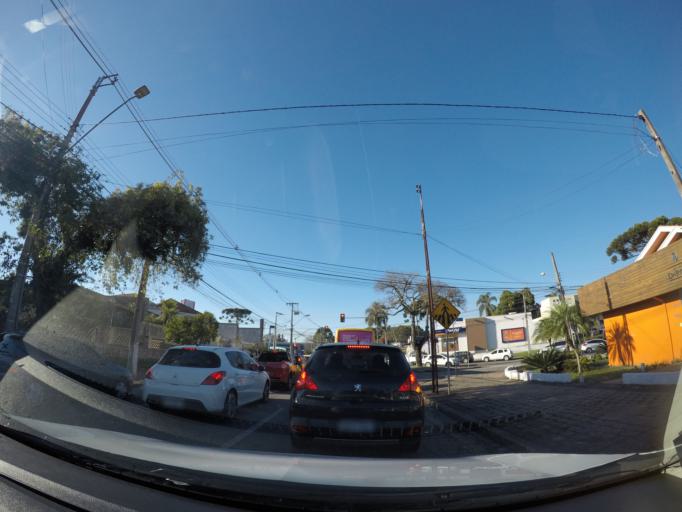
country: BR
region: Parana
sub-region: Curitiba
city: Curitiba
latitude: -25.4100
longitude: -49.2757
